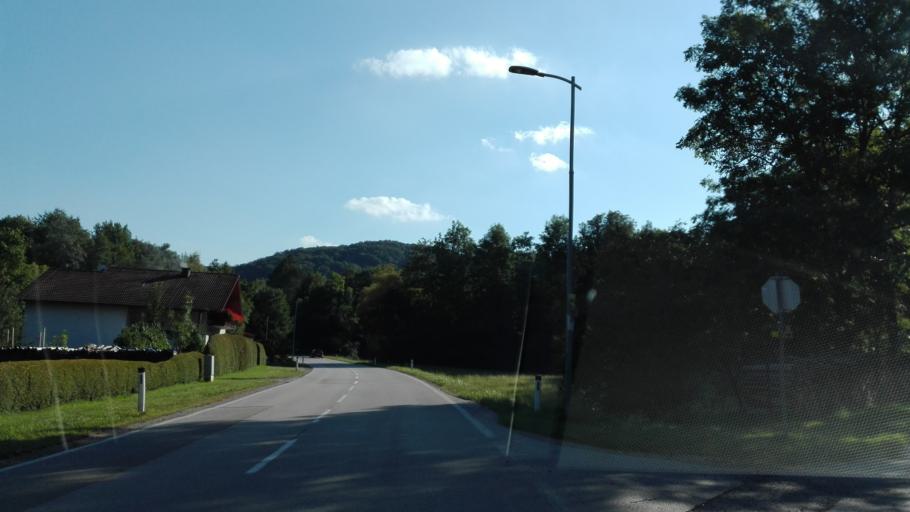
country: AT
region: Lower Austria
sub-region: Politischer Bezirk Sankt Polten
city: Stossing
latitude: 48.1017
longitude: 15.8795
